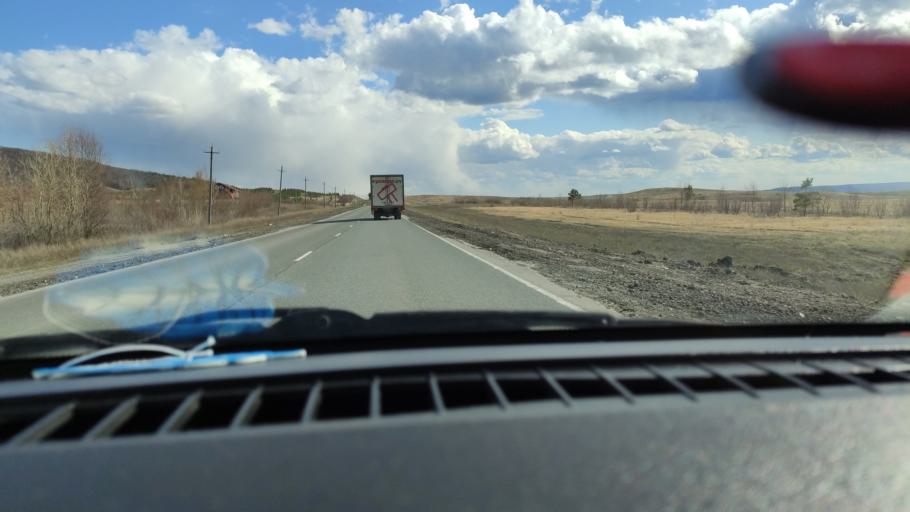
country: RU
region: Saratov
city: Alekseyevka
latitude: 52.3064
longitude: 47.9256
